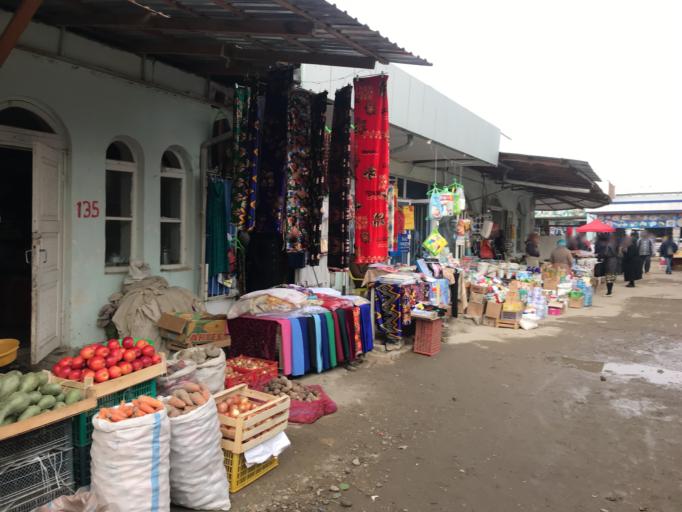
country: UZ
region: Bukhara
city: Kogon
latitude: 39.7256
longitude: 64.5404
